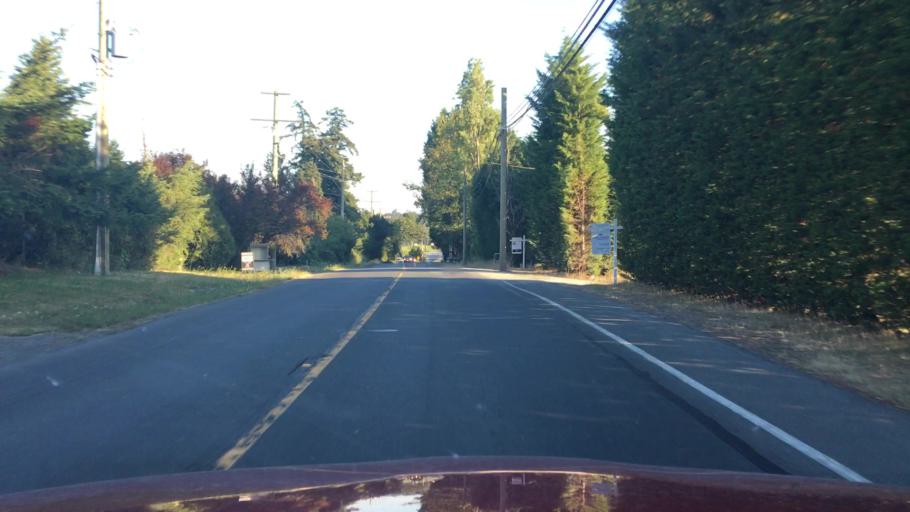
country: CA
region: British Columbia
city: Victoria
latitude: 48.4803
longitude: -123.3546
